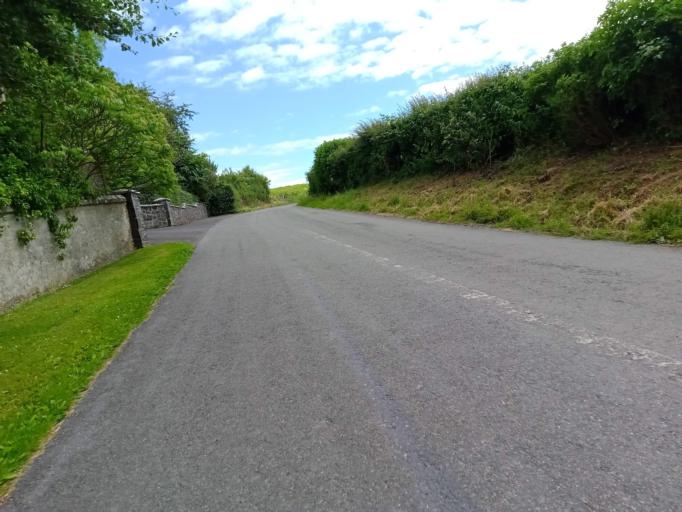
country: IE
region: Leinster
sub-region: Kilkenny
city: Kilkenny
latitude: 52.6819
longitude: -7.2488
